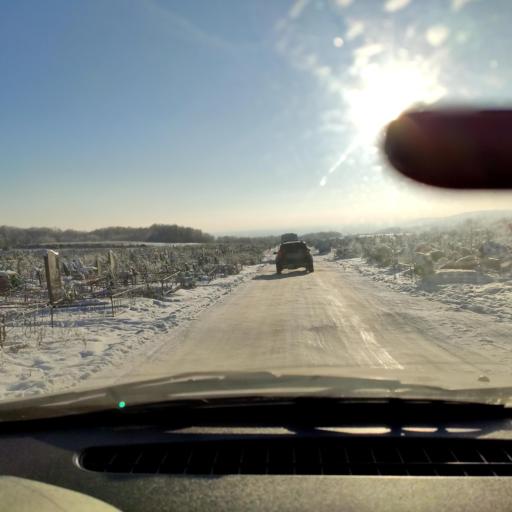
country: RU
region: Bashkortostan
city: Ufa
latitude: 54.8559
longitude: 56.1658
